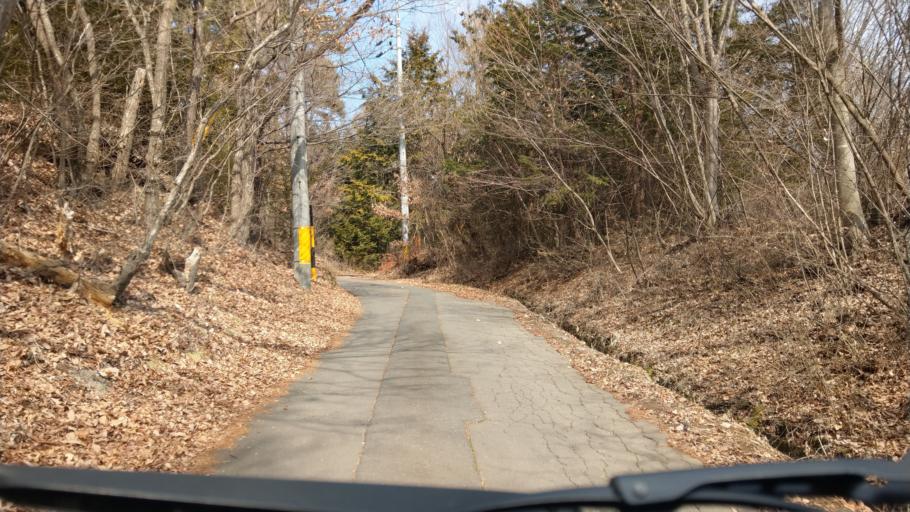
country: JP
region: Nagano
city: Komoro
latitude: 36.3351
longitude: 138.4638
